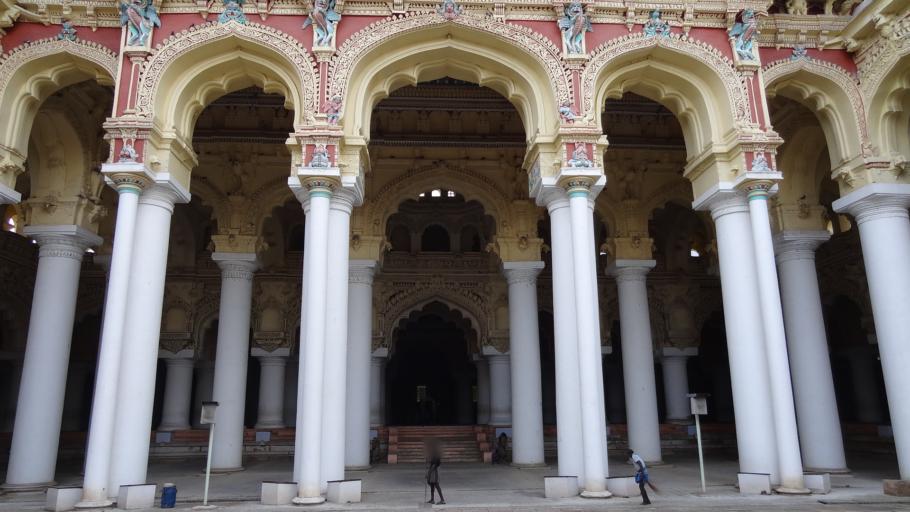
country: IN
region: Tamil Nadu
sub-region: Madurai
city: Madurai
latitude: 9.9149
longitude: 78.1241
